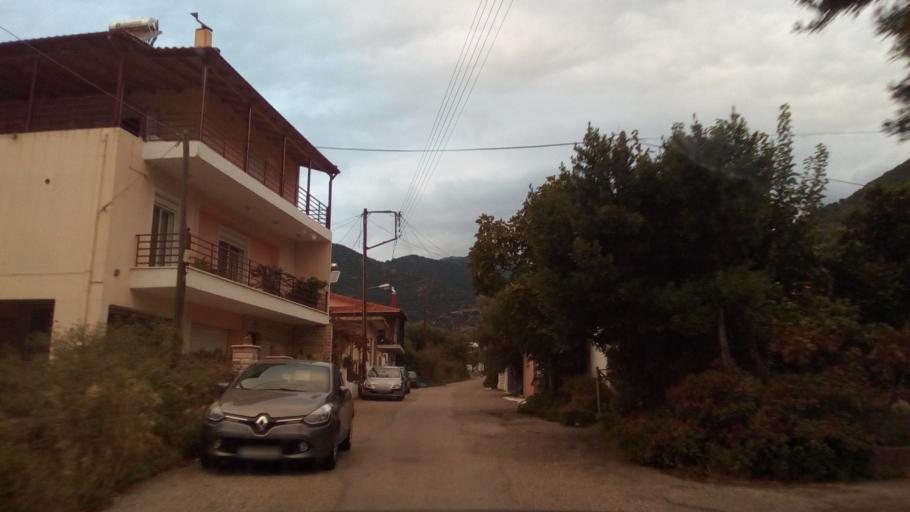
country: GR
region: West Greece
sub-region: Nomos Aitolias kai Akarnanias
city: Nafpaktos
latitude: 38.4101
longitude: 21.8488
